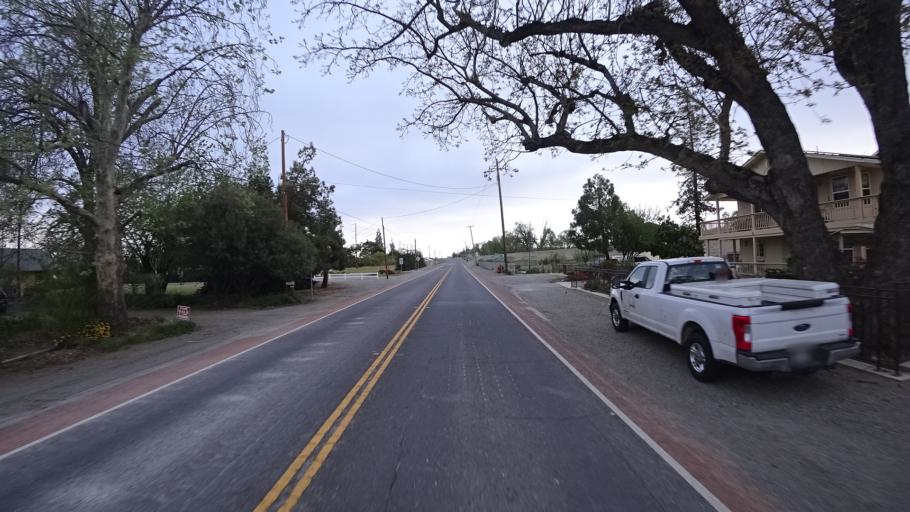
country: US
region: California
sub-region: Colusa County
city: Colusa
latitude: 39.4077
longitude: -122.0096
